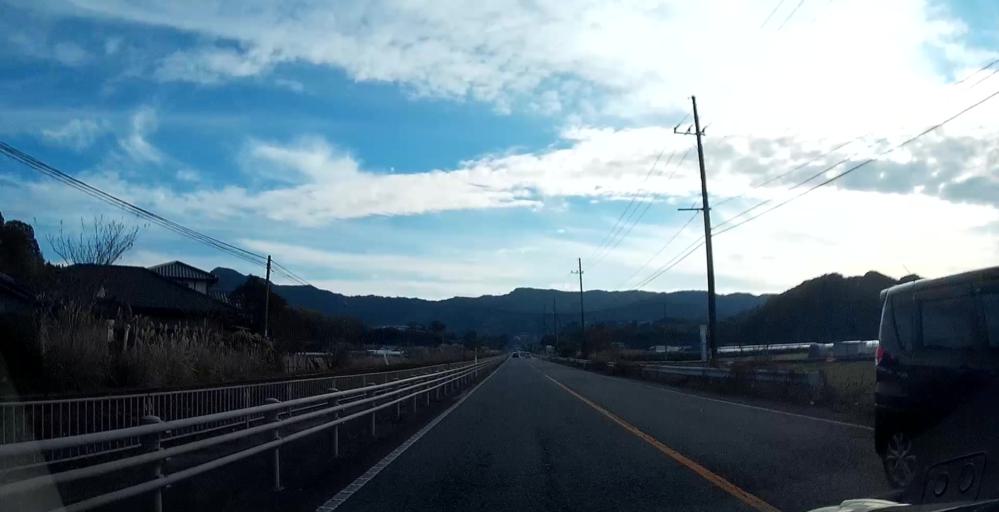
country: JP
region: Kumamoto
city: Uto
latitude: 32.6787
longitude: 130.5534
